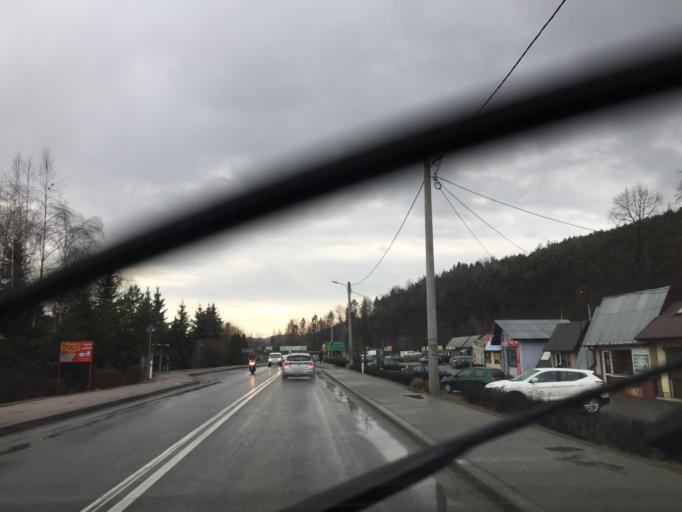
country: PL
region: Lesser Poland Voivodeship
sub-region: Powiat myslenicki
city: Sulkowice
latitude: 49.8551
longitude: 19.7990
